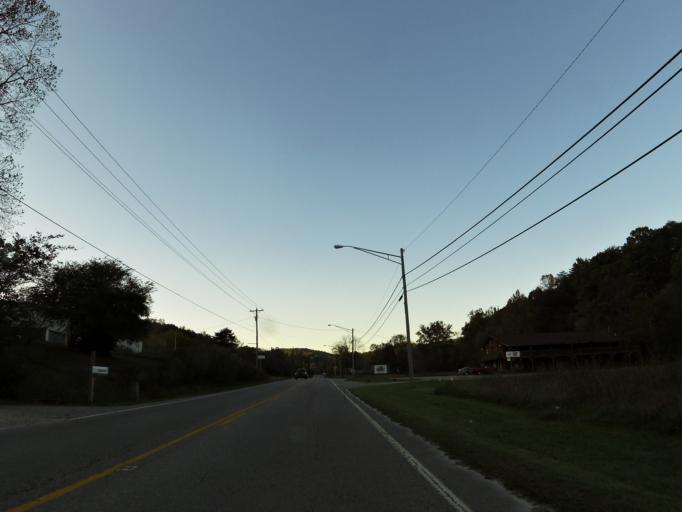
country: US
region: Tennessee
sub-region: Anderson County
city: Rocky Top
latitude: 36.2426
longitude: -84.1657
